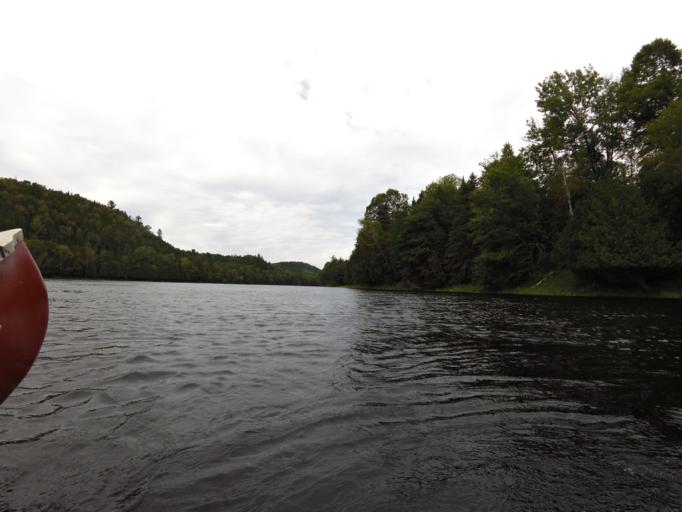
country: CA
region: Quebec
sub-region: Outaouais
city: Wakefield
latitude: 45.7636
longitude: -75.9234
